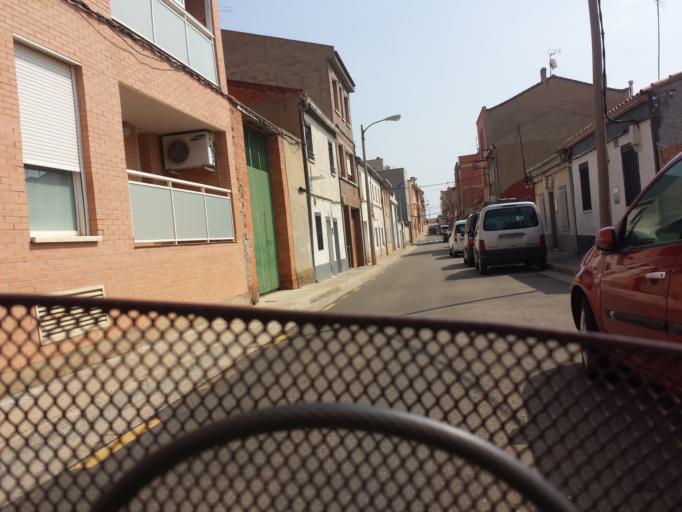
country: ES
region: Aragon
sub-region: Provincia de Zaragoza
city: Oliver-Valdefierro, Oliver, Valdefierro
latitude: 41.6370
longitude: -0.9344
